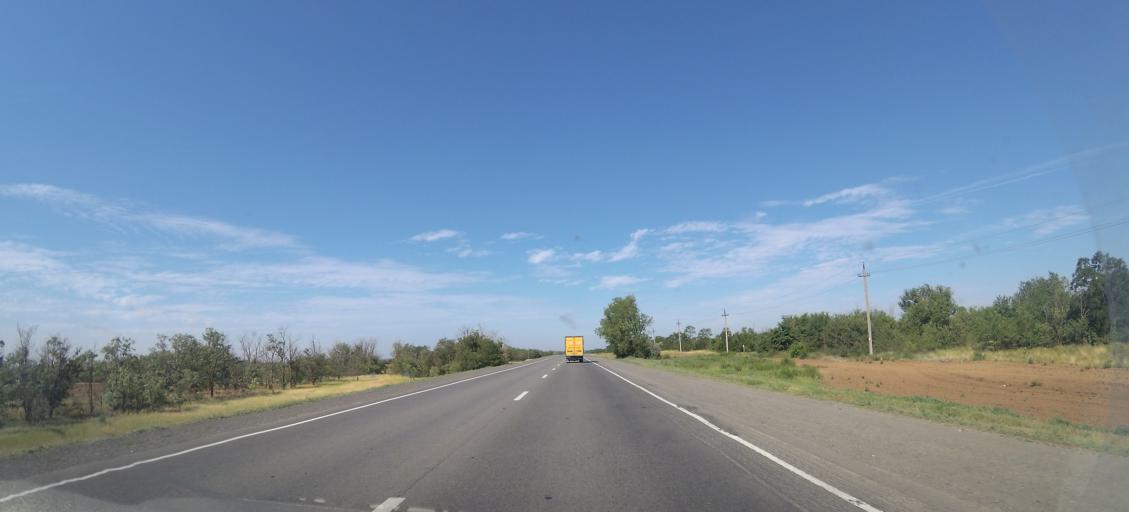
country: RU
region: Volgograd
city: Oktyabr'skiy
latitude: 48.6953
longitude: 43.7932
